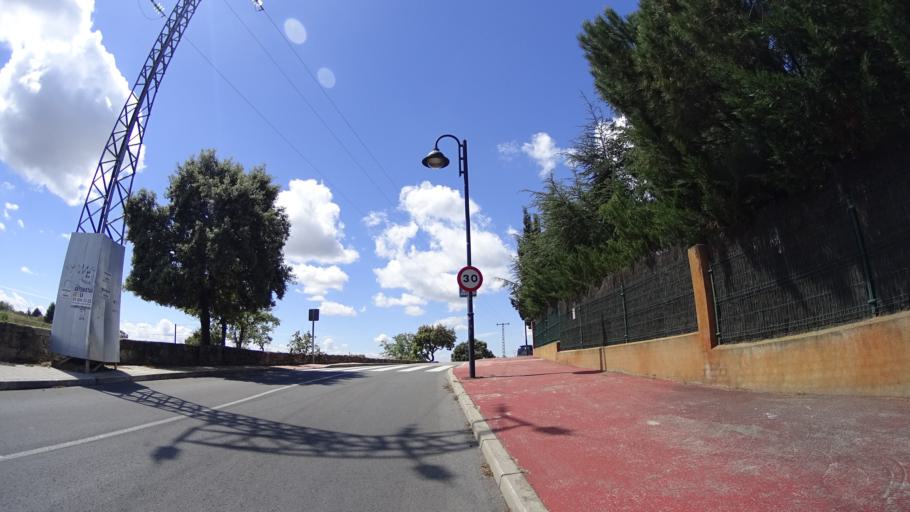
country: ES
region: Madrid
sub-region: Provincia de Madrid
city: Galapagar
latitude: 40.5699
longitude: -4.0077
